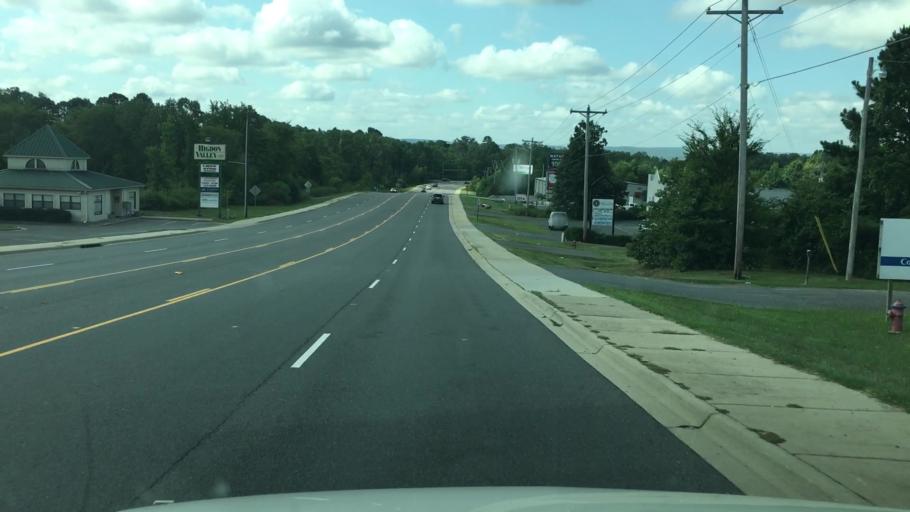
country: US
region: Arkansas
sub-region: Garland County
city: Lake Hamilton
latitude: 34.4590
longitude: -93.0774
